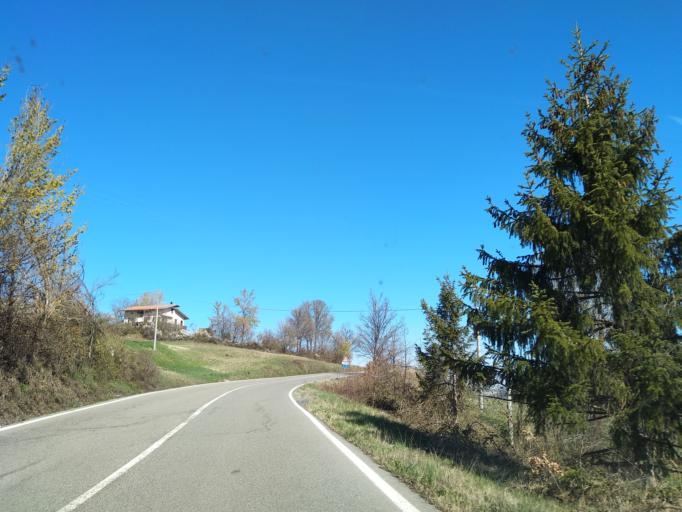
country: IT
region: Emilia-Romagna
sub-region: Provincia di Reggio Emilia
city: Castelnovo ne'Monti
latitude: 44.4207
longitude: 10.3710
